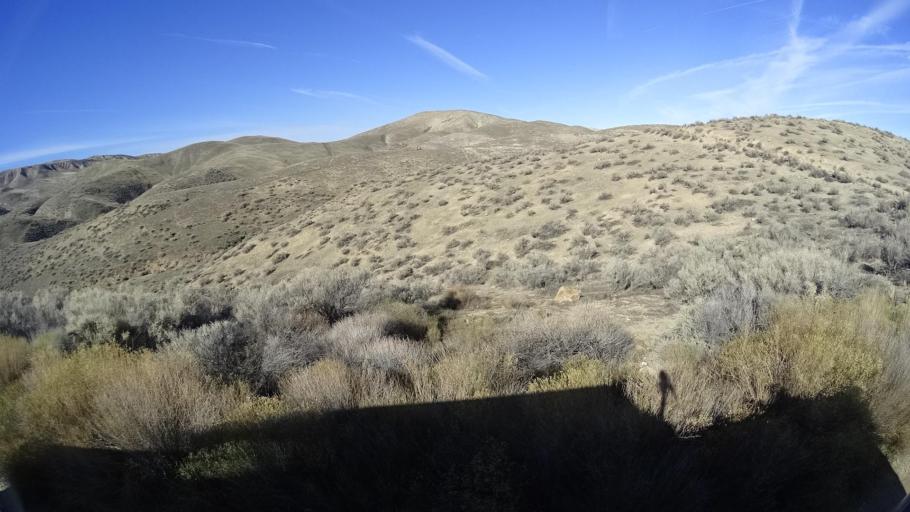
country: US
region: California
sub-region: Kern County
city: Maricopa
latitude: 35.0151
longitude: -119.4725
